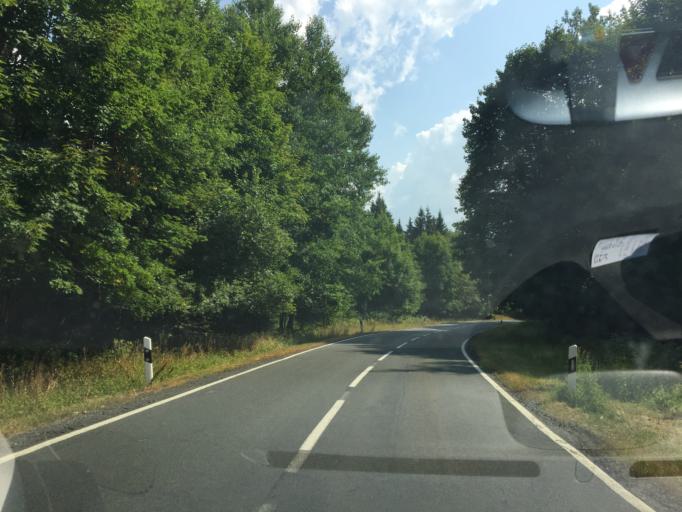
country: DE
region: Saxony-Anhalt
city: Benneckenstein
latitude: 51.6636
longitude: 10.6881
